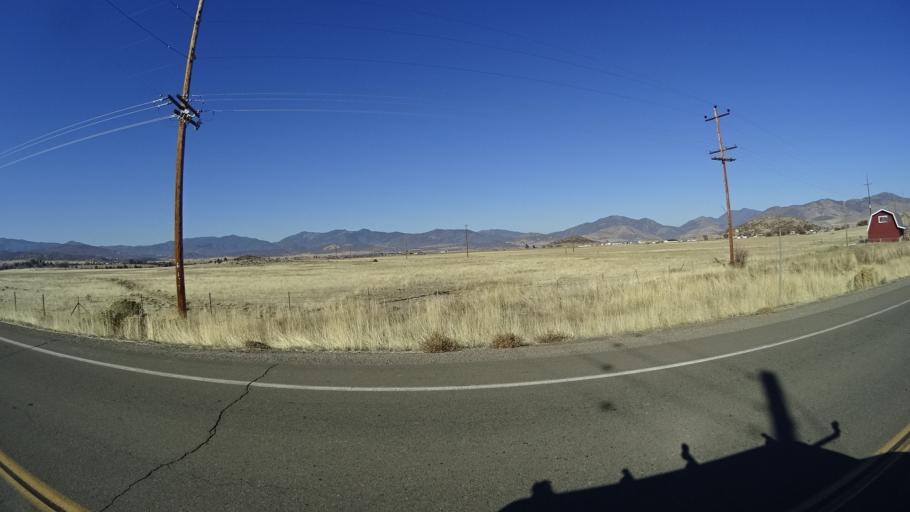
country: US
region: California
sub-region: Siskiyou County
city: Montague
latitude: 41.7192
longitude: -122.5347
